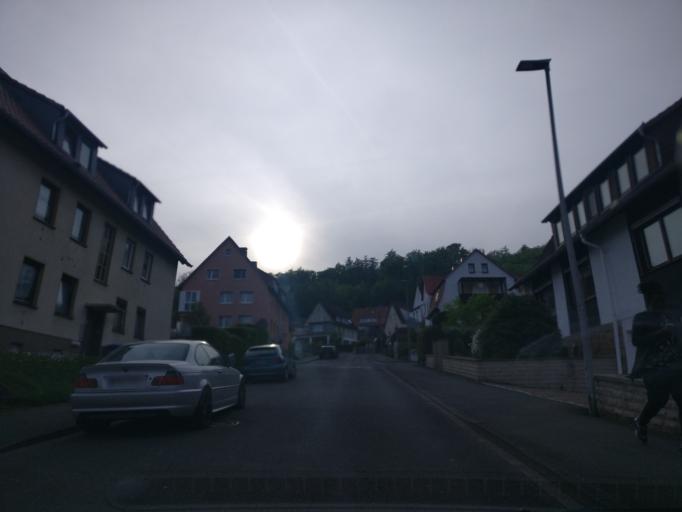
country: DE
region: Lower Saxony
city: Hannoversch Munden
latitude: 51.4103
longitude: 9.6389
